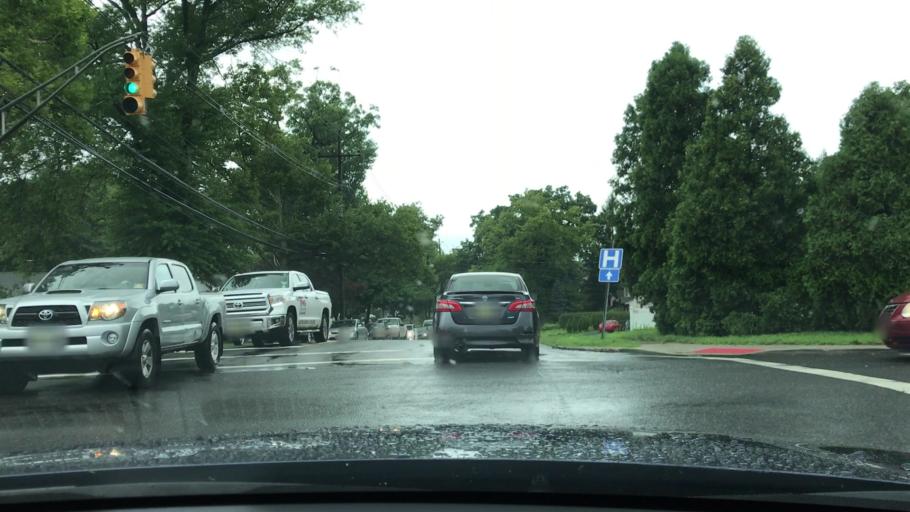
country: US
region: New Jersey
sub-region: Bergen County
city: Oradell
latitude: 40.9593
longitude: -74.0507
